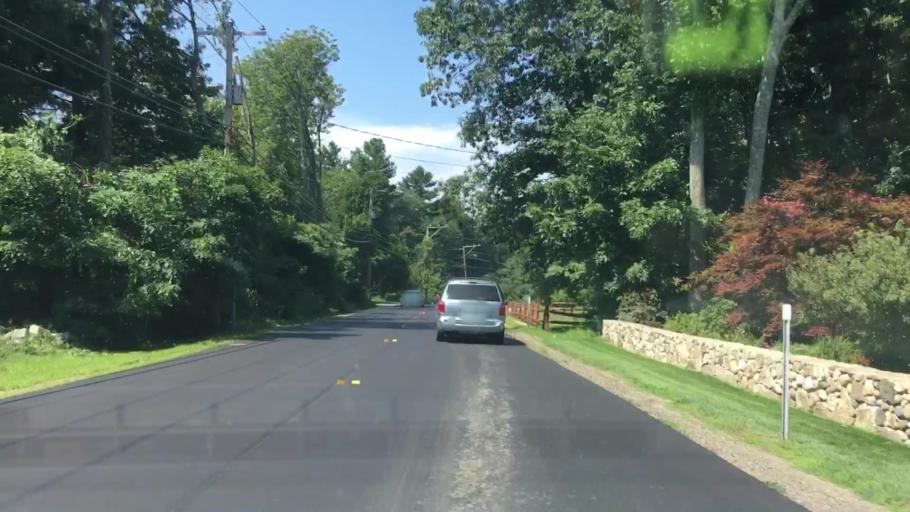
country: US
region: New Hampshire
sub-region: Rockingham County
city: Hampstead
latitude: 42.8889
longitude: -71.1996
